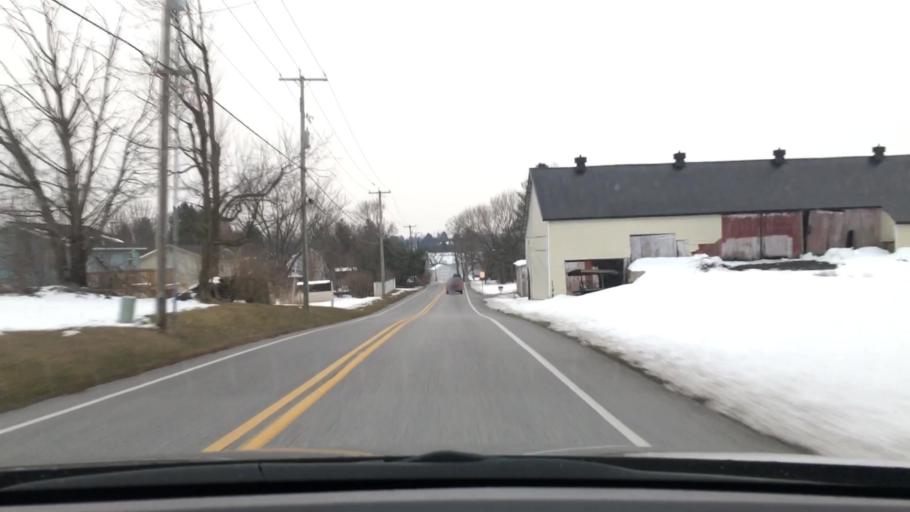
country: US
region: Pennsylvania
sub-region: York County
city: Weigelstown
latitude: 39.9616
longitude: -76.8391
